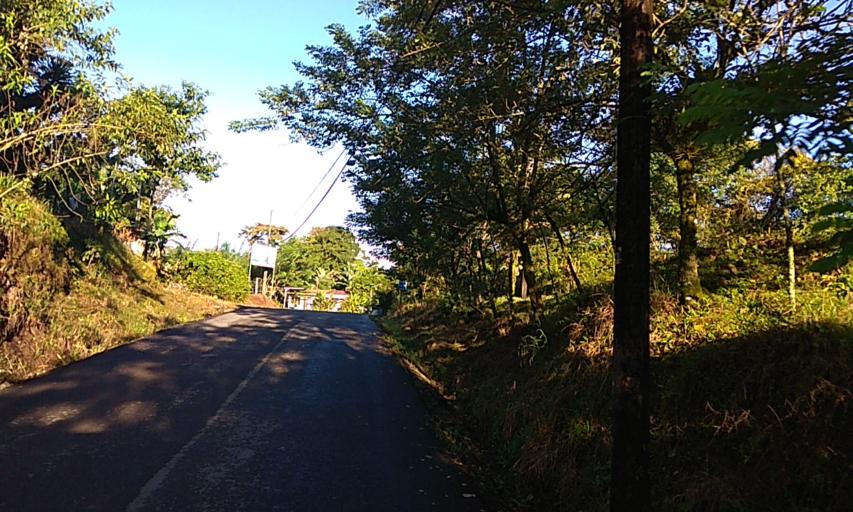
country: CR
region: Limon
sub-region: Canton de Pococi
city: Guapiles
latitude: 10.1635
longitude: -83.8086
